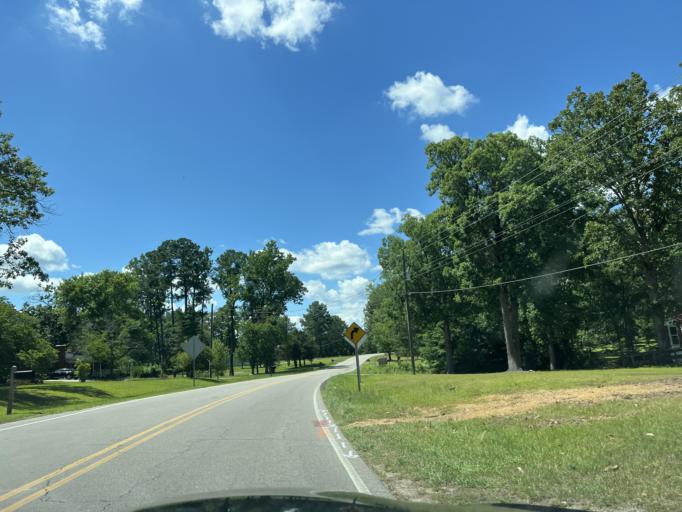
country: US
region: North Carolina
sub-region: Lee County
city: Sanford
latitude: 35.4387
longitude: -79.1717
